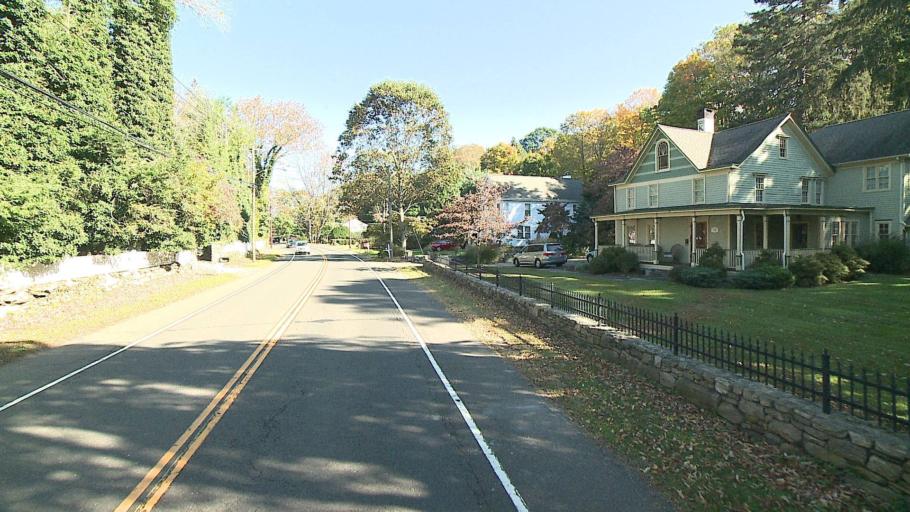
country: US
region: Connecticut
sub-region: Fairfield County
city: Westport
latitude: 41.1362
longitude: -73.3548
